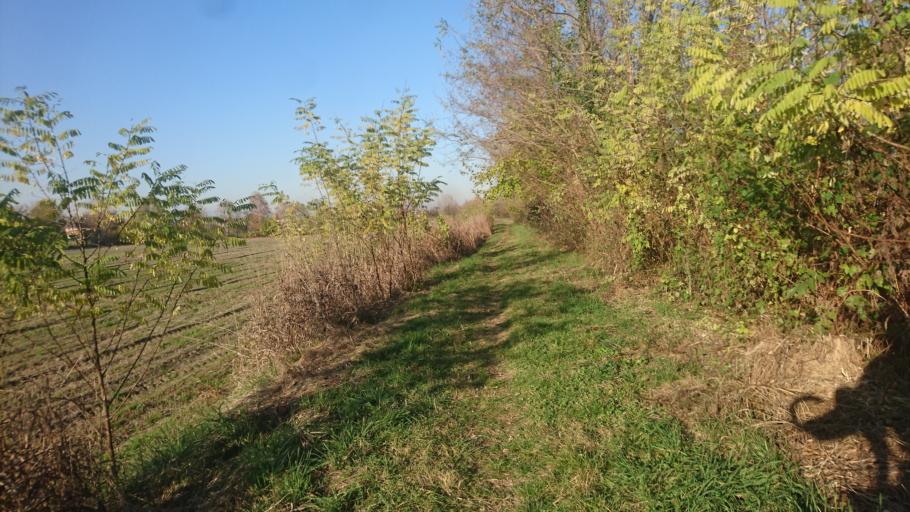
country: IT
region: Veneto
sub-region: Provincia di Padova
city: Villaguattera
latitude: 45.4408
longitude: 11.8286
